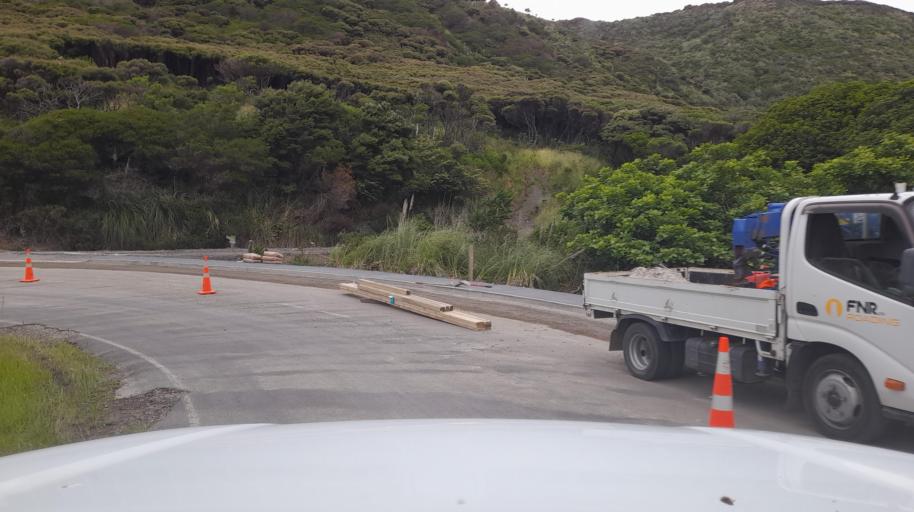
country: NZ
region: Northland
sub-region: Far North District
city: Ahipara
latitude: -35.1816
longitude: 173.1270
